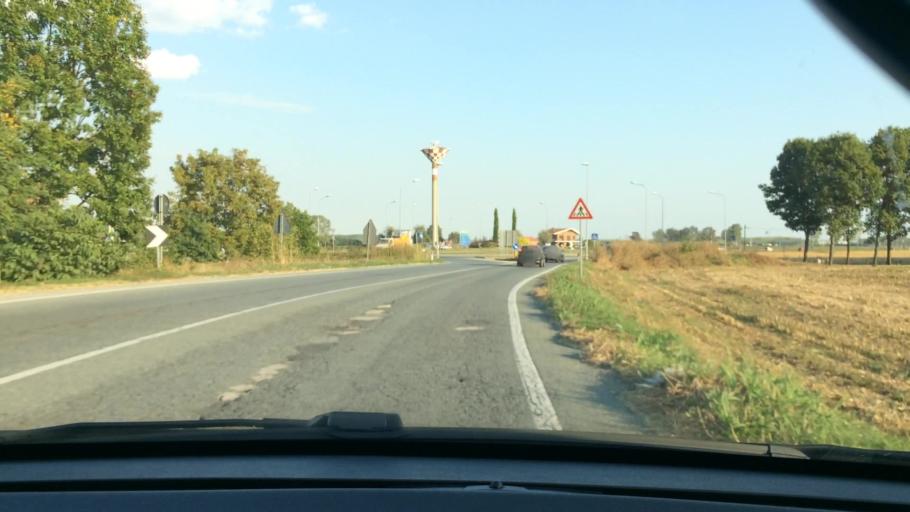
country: IT
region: Piedmont
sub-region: Provincia di Torino
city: Candiolo
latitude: 44.9544
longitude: 7.5957
